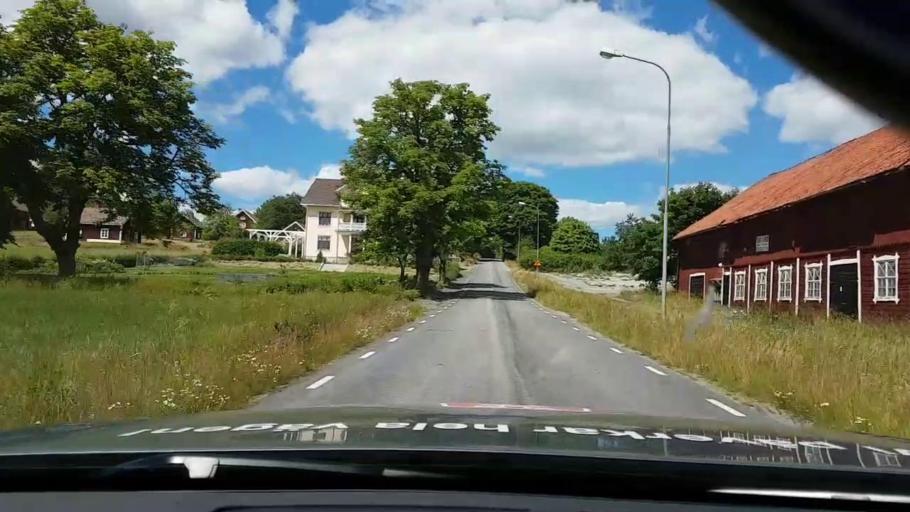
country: SE
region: Kalmar
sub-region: Vasterviks Kommun
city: Forserum
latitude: 58.0077
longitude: 16.5810
